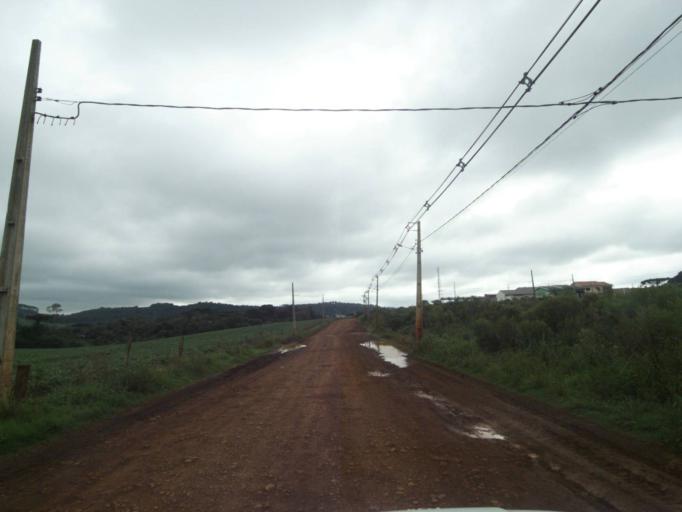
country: BR
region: Parana
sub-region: Pitanga
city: Pitanga
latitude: -24.9408
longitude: -51.8781
